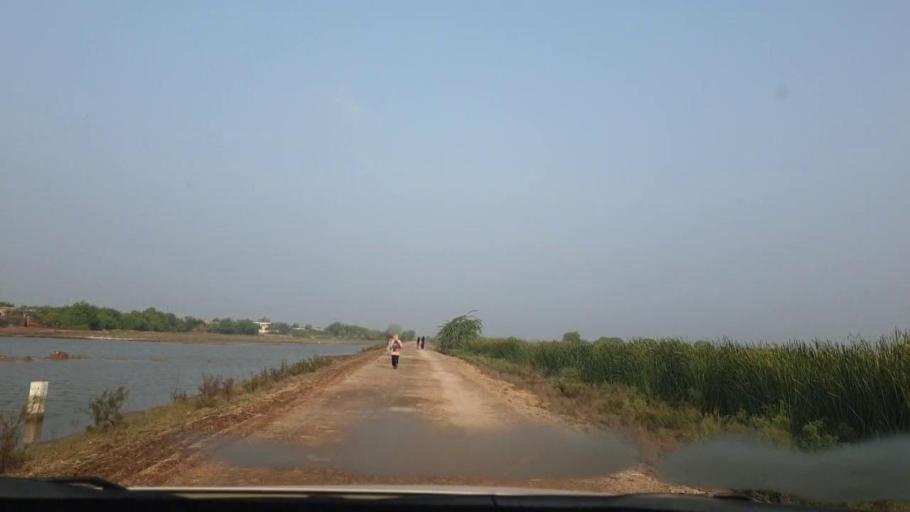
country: PK
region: Sindh
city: Tando Muhammad Khan
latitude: 25.0901
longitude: 68.4810
